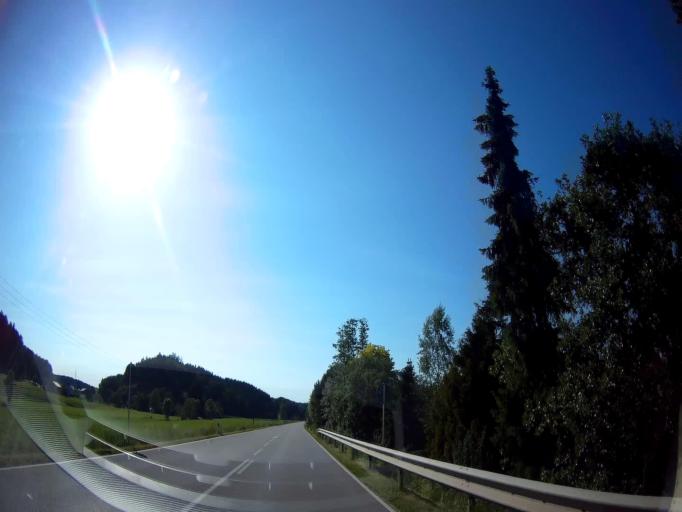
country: DE
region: Bavaria
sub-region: Lower Bavaria
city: Zeilarn
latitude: 48.2954
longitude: 12.8465
